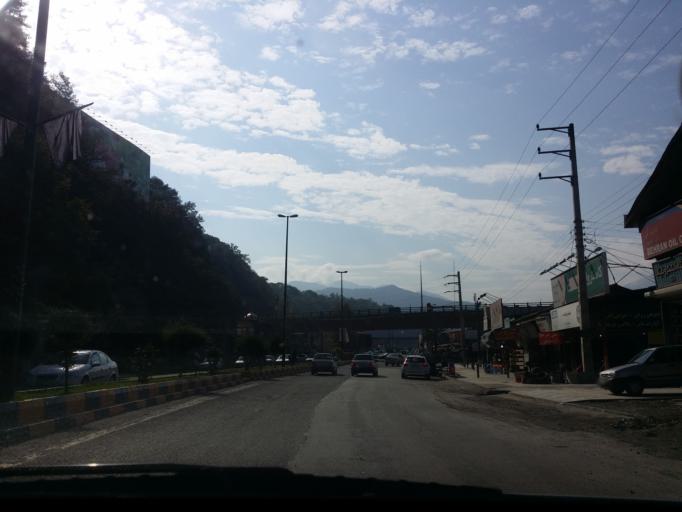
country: IR
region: Mazandaran
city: Chalus
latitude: 36.6475
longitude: 51.4139
